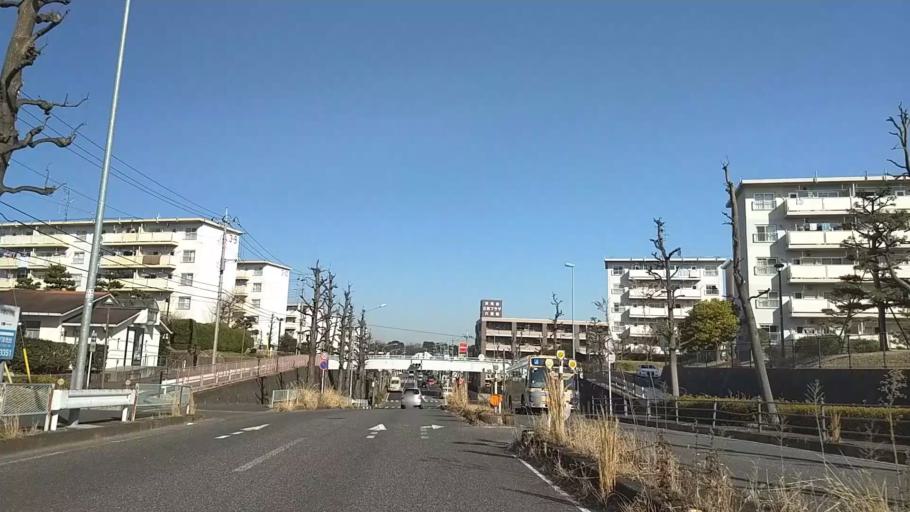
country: JP
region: Kanagawa
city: Yokohama
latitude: 35.3826
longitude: 139.5928
